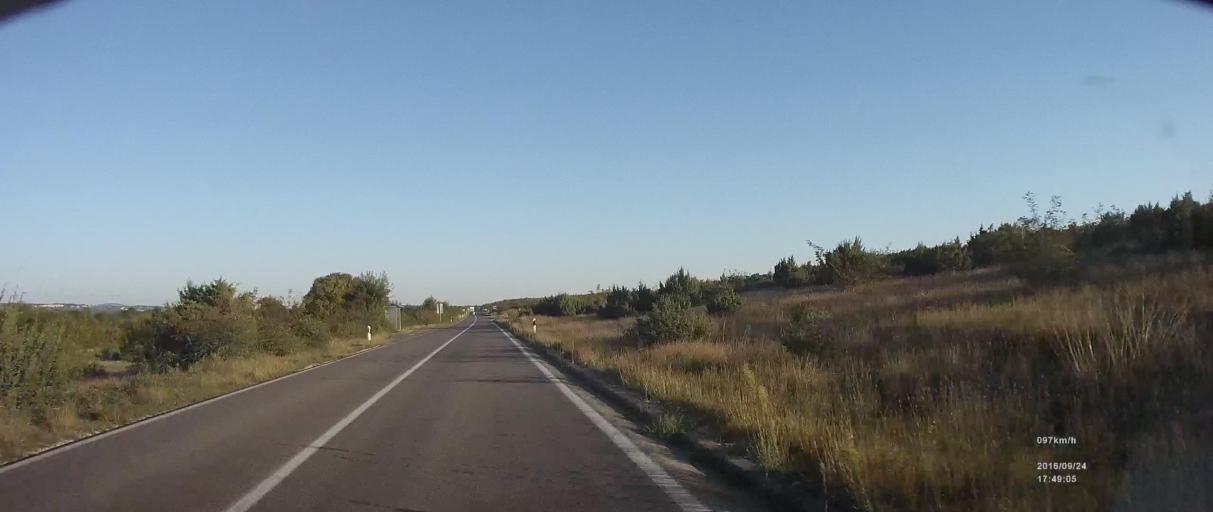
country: HR
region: Zadarska
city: Polaca
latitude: 44.0576
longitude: 15.5453
